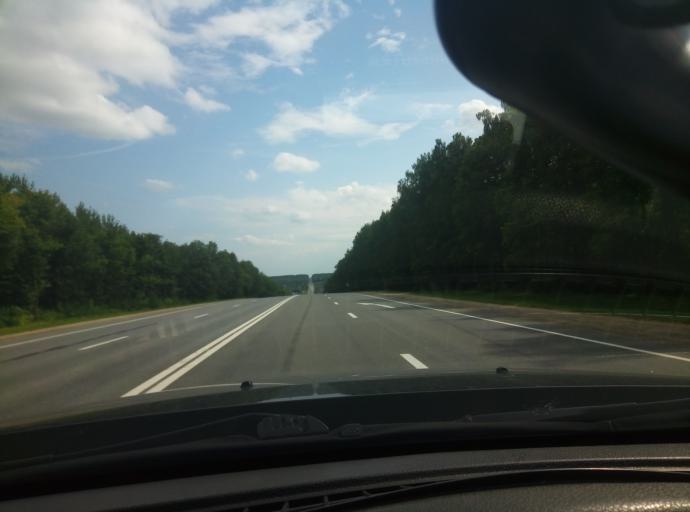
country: RU
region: Tula
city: Gorelki
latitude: 54.3140
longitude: 37.5648
